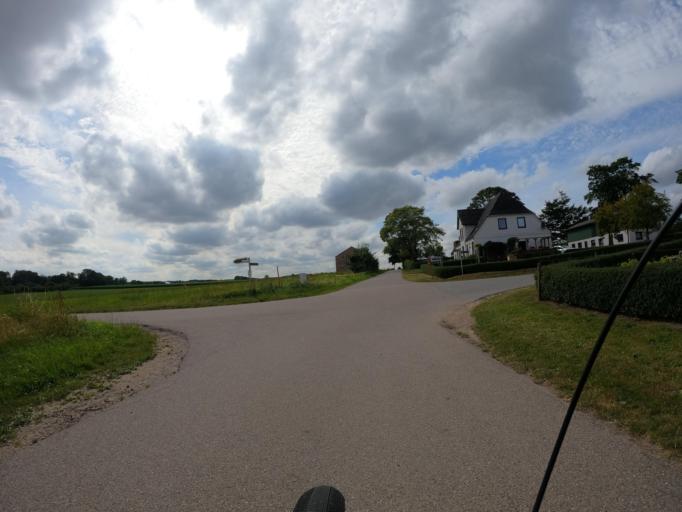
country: DE
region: Schleswig-Holstein
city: Steinberg
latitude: 54.7443
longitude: 9.7838
